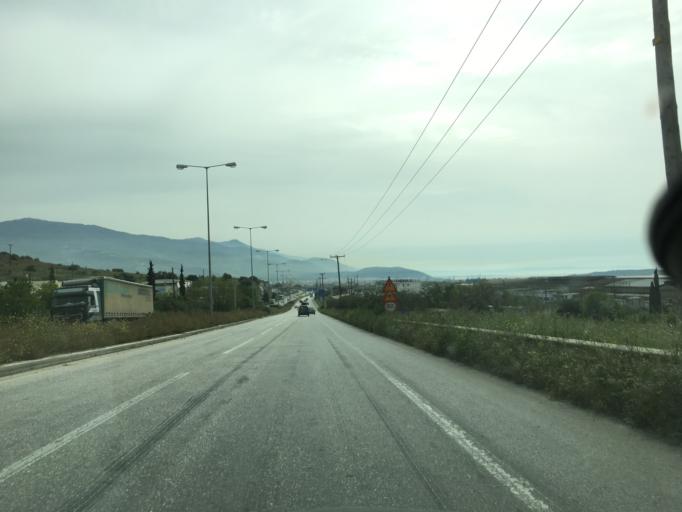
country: GR
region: Thessaly
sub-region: Nomos Magnisias
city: Nea Ionia
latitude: 39.3765
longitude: 22.8897
